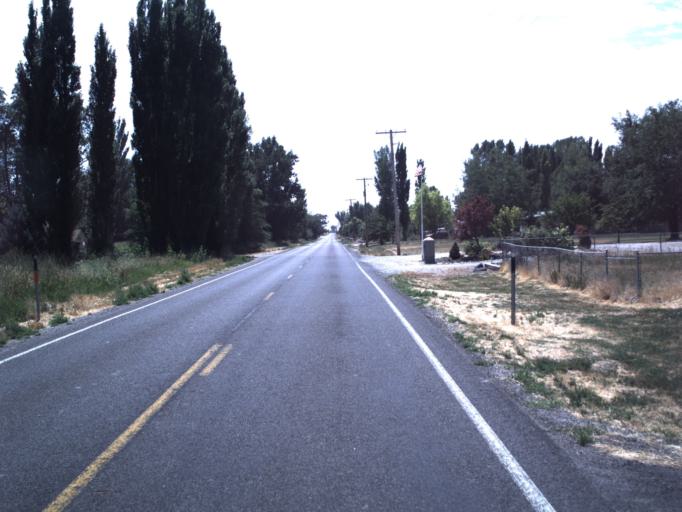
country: US
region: Utah
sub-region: Box Elder County
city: Tremonton
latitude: 41.6786
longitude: -112.2968
